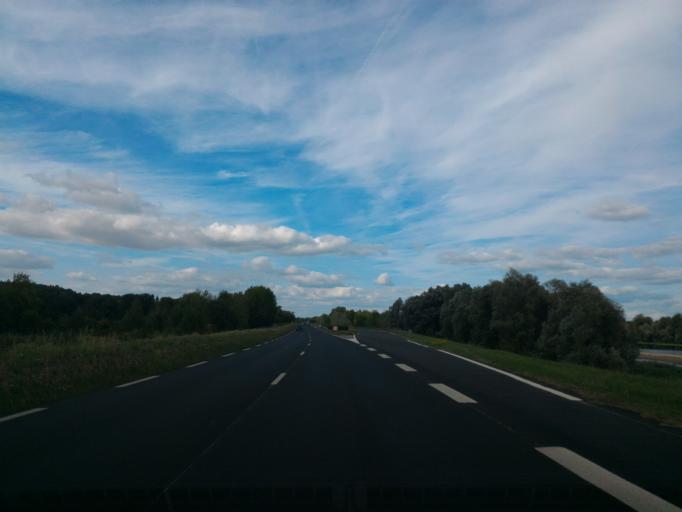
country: FR
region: Centre
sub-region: Departement du Loir-et-Cher
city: Chailles
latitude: 47.5390
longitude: 1.2801
